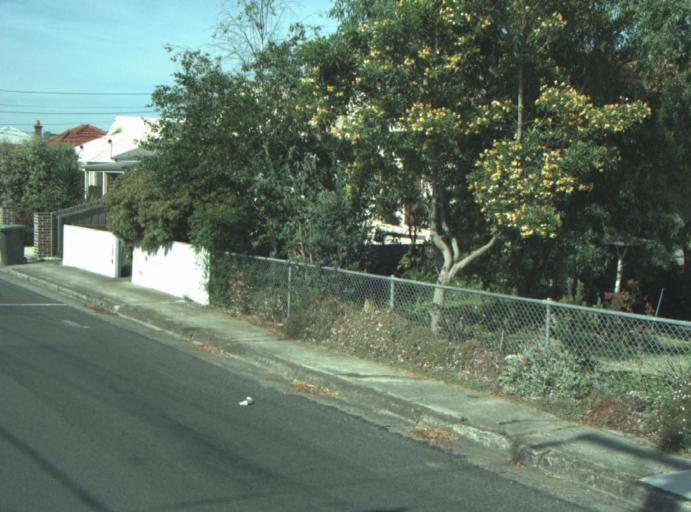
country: AU
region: Victoria
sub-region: Greater Geelong
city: Geelong West
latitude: -38.1411
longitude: 144.3398
